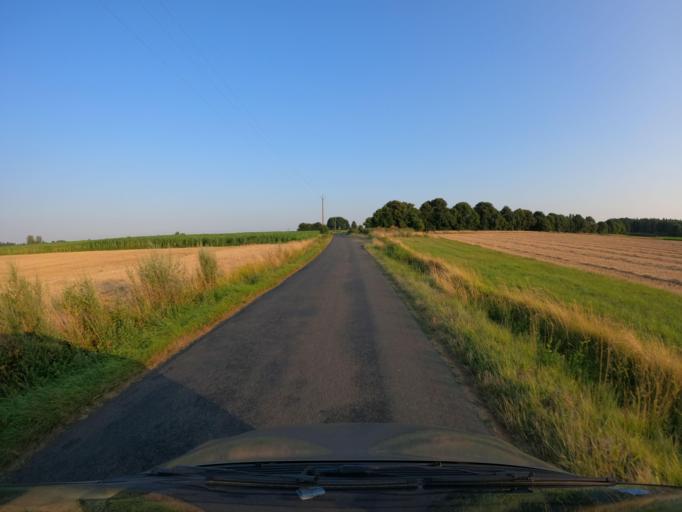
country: FR
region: Pays de la Loire
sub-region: Departement de la Sarthe
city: Parce-sur-Sarthe
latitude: 47.8932
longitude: -0.2182
